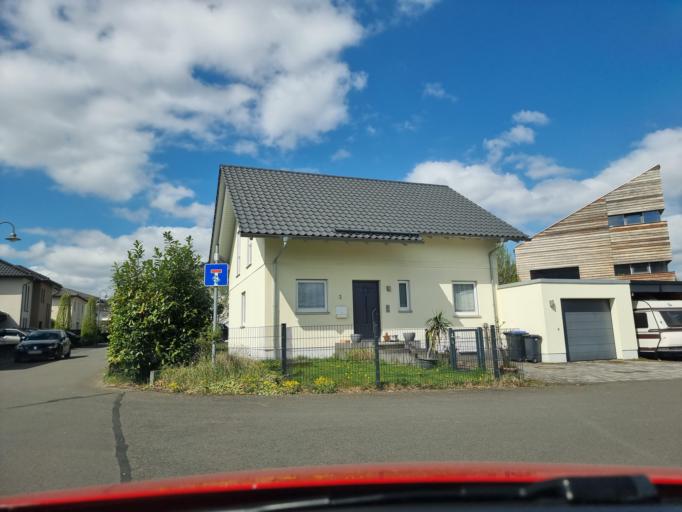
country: DE
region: Rheinland-Pfalz
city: Longuich
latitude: 49.7908
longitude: 6.7966
